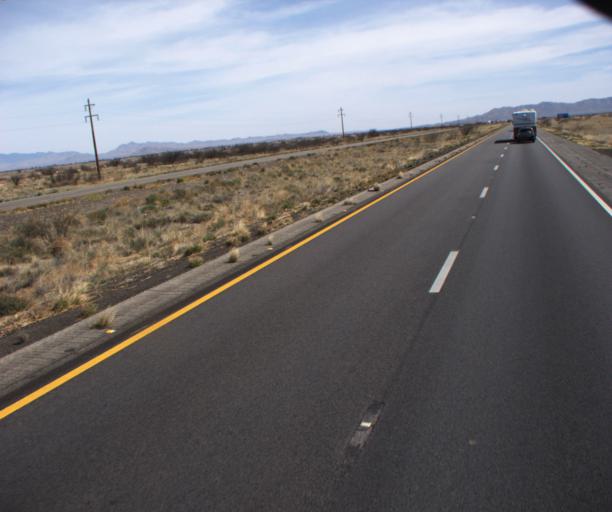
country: US
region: Arizona
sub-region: Cochise County
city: Willcox
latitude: 32.2026
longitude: -109.9053
